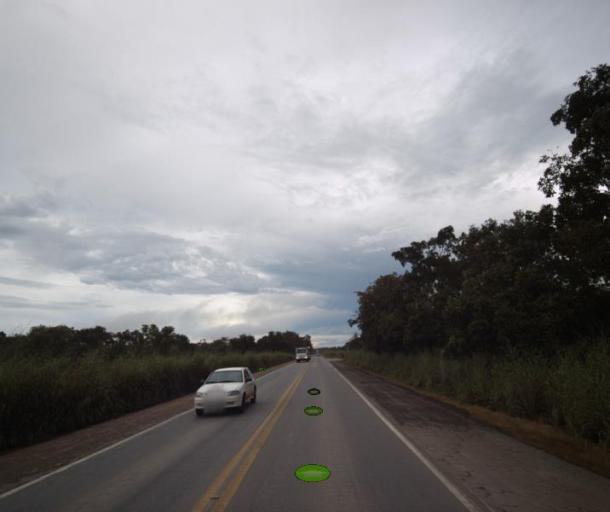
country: BR
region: Goias
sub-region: Porangatu
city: Porangatu
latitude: -13.5515
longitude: -49.0952
